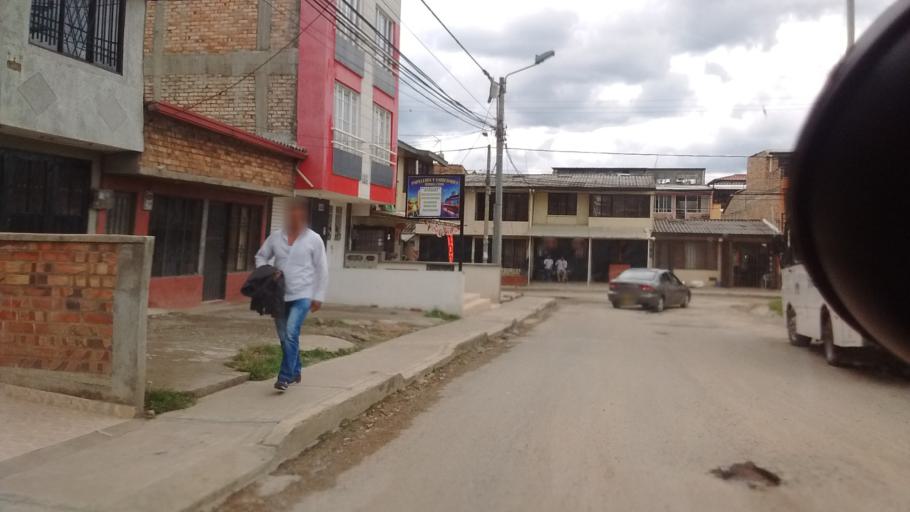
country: CO
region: Cauca
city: Popayan
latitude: 2.4743
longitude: -76.5573
